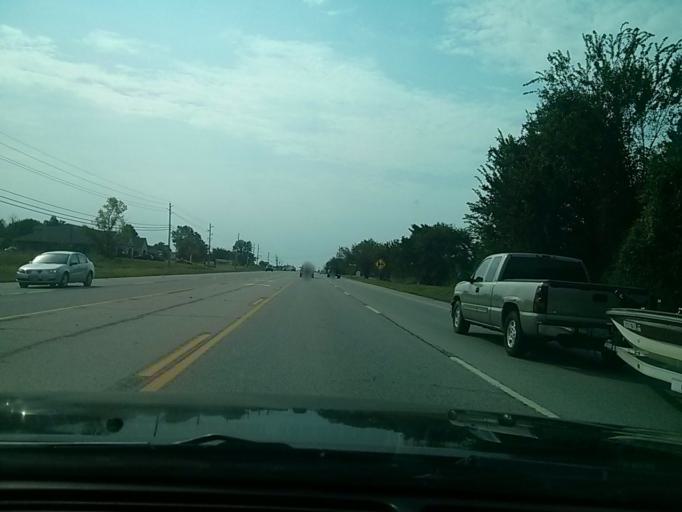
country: US
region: Oklahoma
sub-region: Wagoner County
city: Coweta
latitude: 35.9811
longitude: -95.6666
